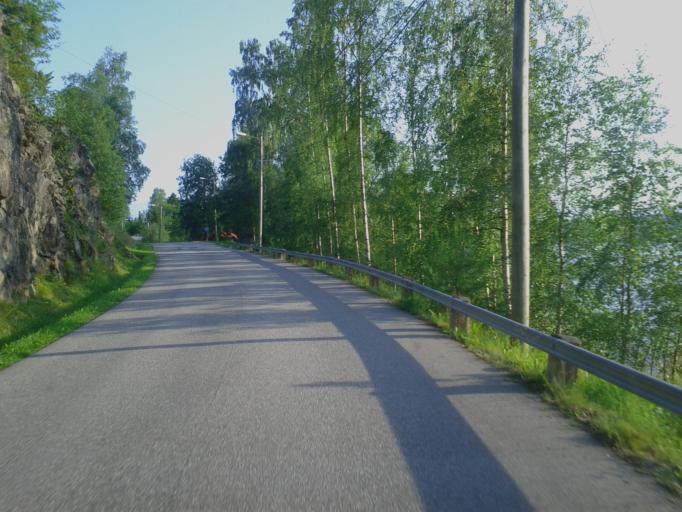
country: SE
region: Vaesternorrland
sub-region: OErnskoeldsviks Kommun
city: Ornskoldsvik
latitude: 63.2650
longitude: 18.8071
